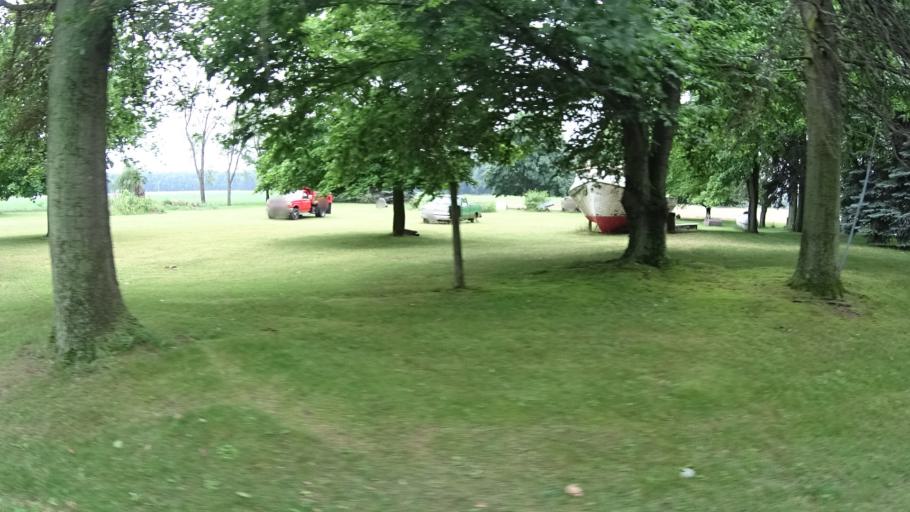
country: US
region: Ohio
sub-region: Erie County
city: Milan
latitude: 41.2944
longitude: -82.5541
